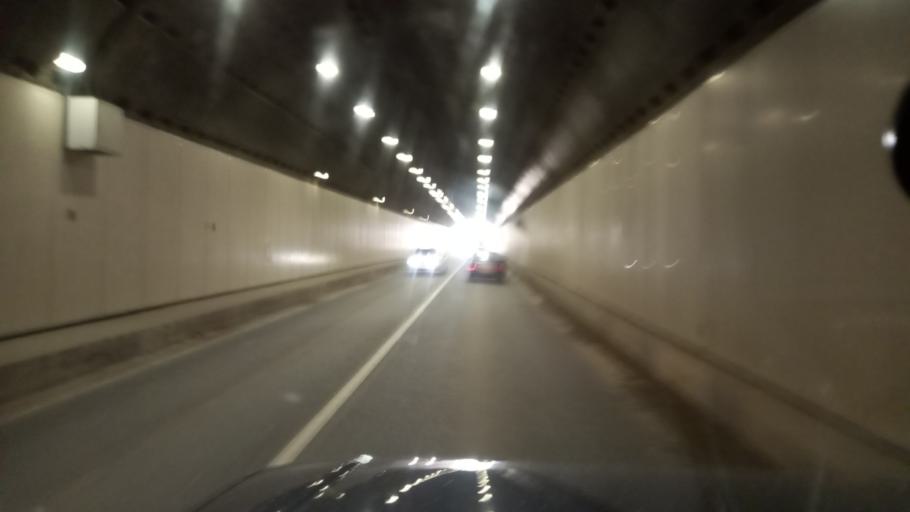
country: RU
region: Dagestan
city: Derbent
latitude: 42.0550
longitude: 48.2787
